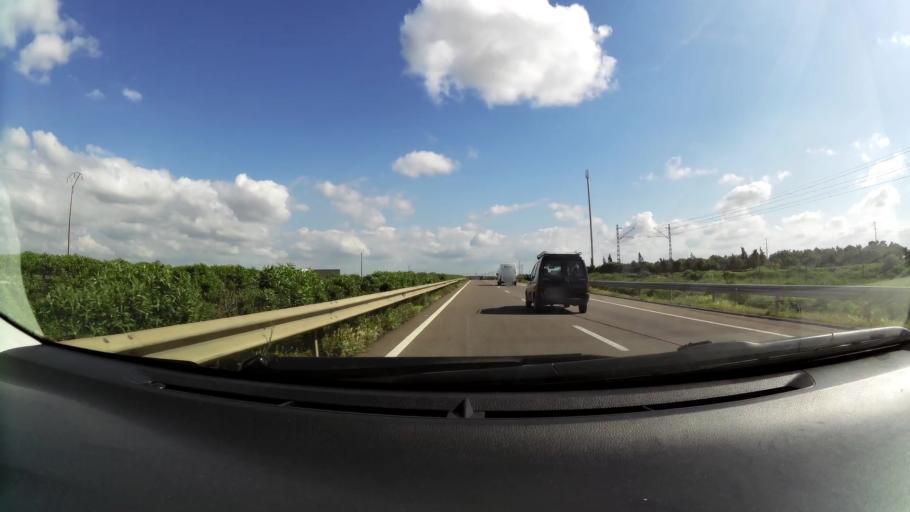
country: MA
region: Chaouia-Ouardigha
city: Nouaseur
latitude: 33.3450
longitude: -7.6138
